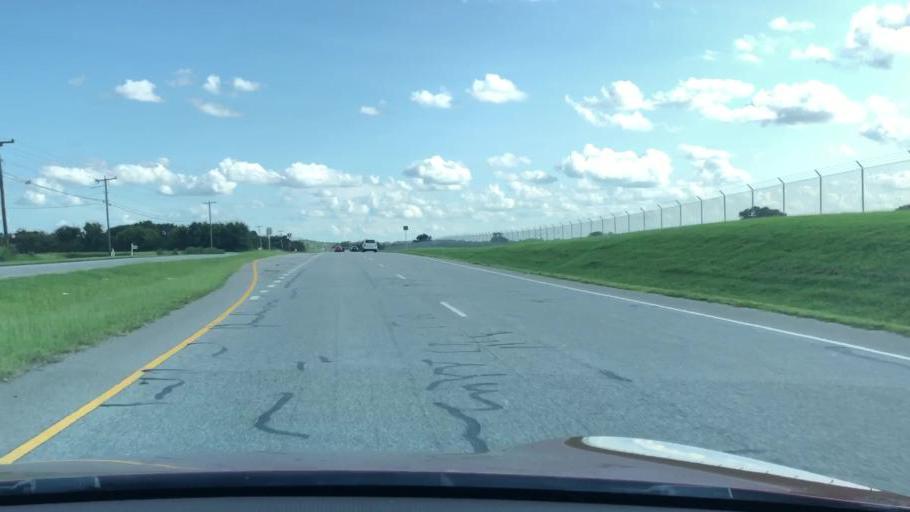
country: US
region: Virginia
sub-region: City of Virginia Beach
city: Virginia Beach
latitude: 36.8252
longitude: -76.0096
